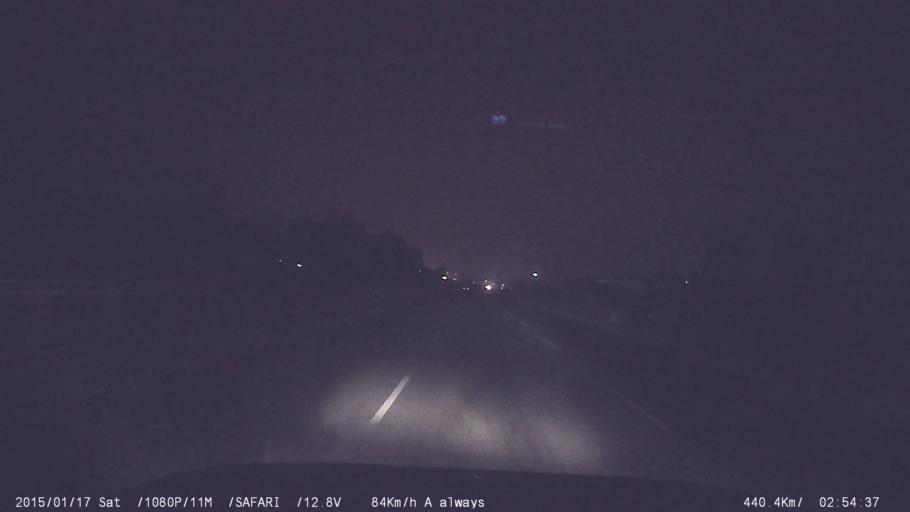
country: IN
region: Tamil Nadu
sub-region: Krishnagiri
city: Hosur
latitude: 12.7824
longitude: 77.7615
